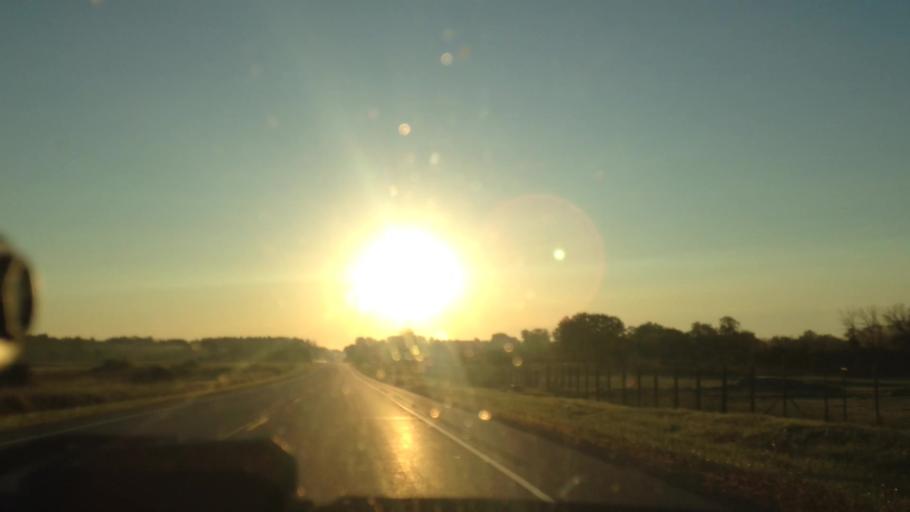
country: US
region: Wisconsin
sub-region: Washington County
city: West Bend
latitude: 43.4264
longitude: -88.1222
